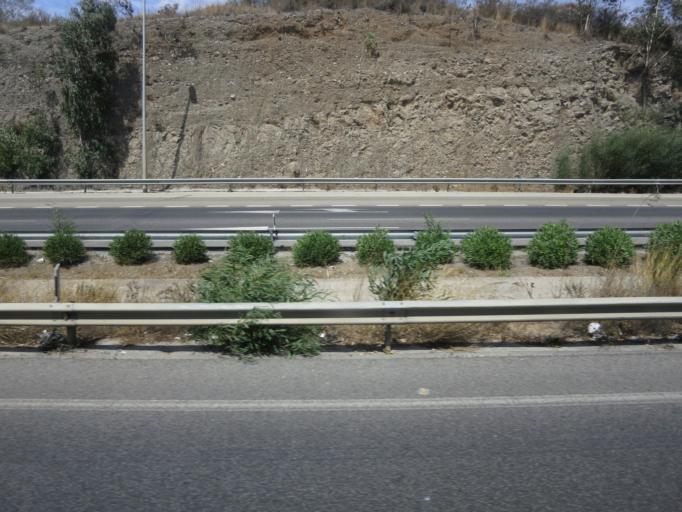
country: ES
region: Andalusia
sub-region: Provincia de Malaga
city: Marbella
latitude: 36.5114
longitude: -4.9471
